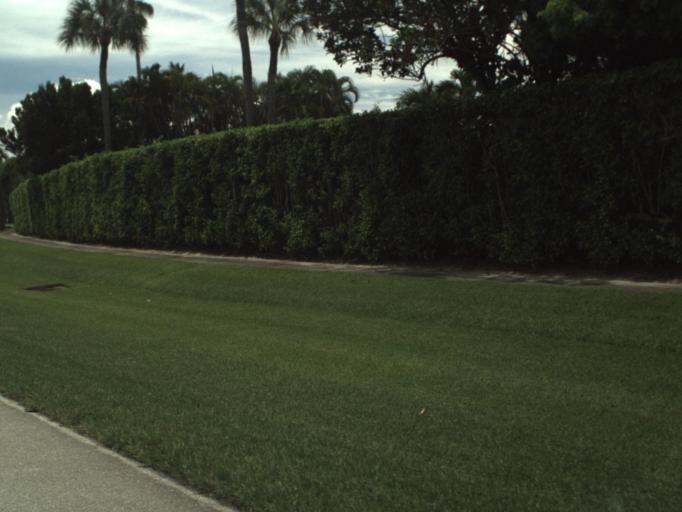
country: US
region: Florida
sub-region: Palm Beach County
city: Juno Beach
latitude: 26.8427
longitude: -80.0510
